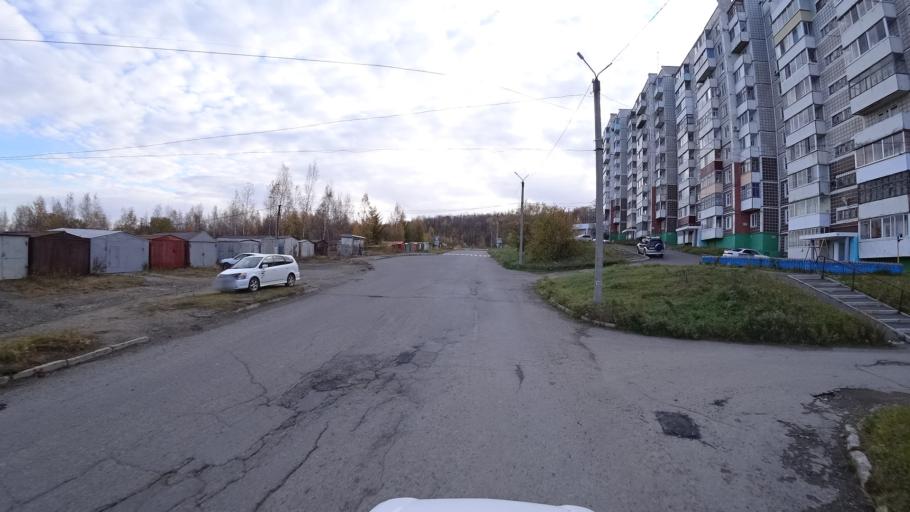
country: RU
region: Khabarovsk Krai
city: Amursk
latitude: 50.2489
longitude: 136.9209
